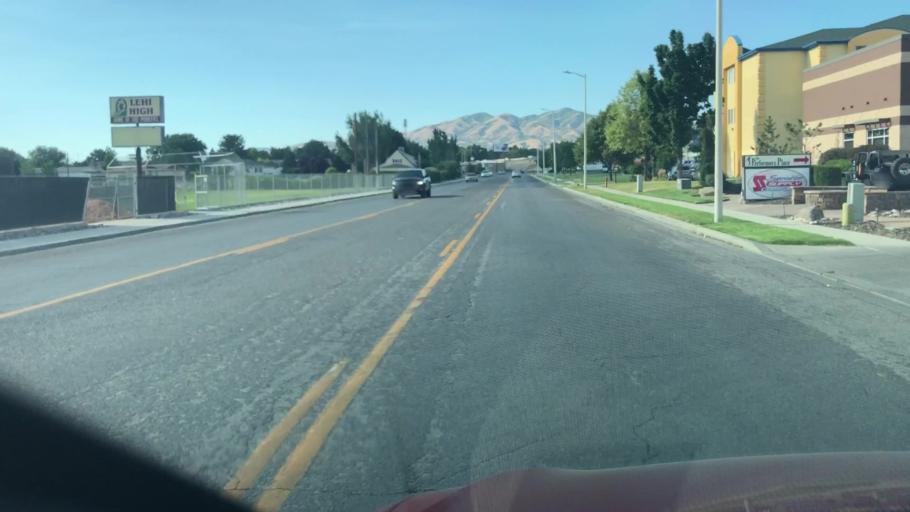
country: US
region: Utah
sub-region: Utah County
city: Lehi
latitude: 40.3900
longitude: -111.8363
